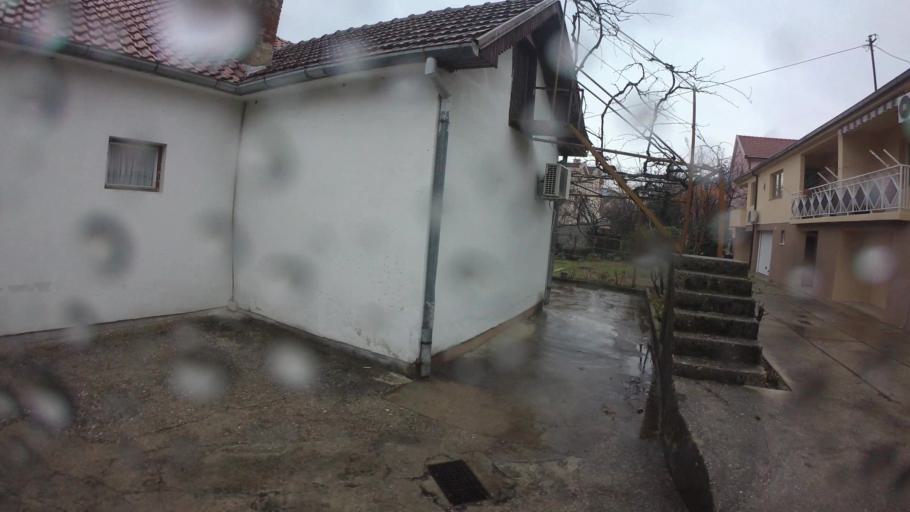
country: BA
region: Federation of Bosnia and Herzegovina
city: Cim
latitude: 43.3485
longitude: 17.7848
